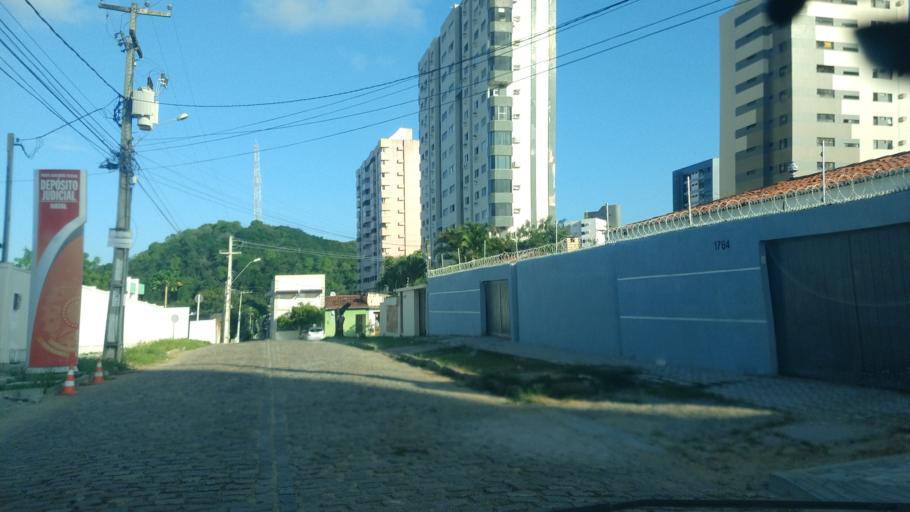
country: BR
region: Rio Grande do Norte
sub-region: Natal
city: Natal
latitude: -5.8121
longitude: -35.1992
